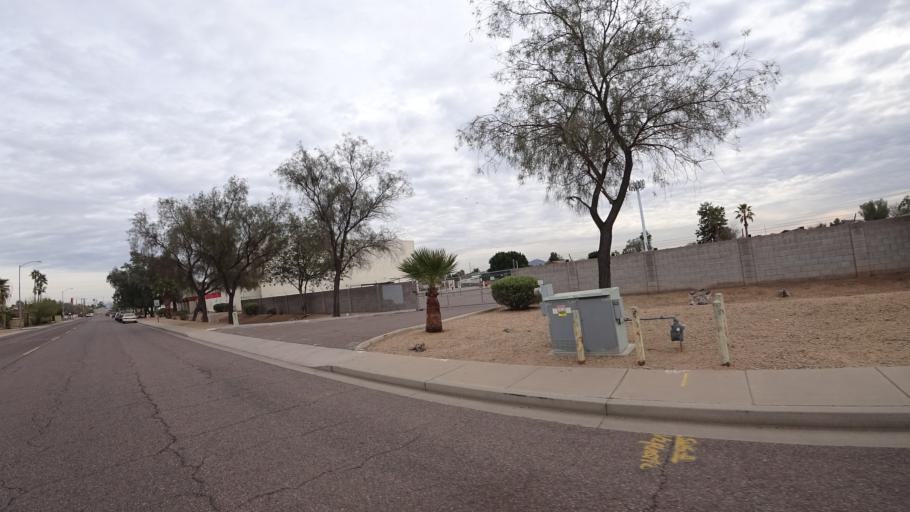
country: US
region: Arizona
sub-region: Maricopa County
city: Glendale
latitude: 33.6473
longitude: -112.1196
